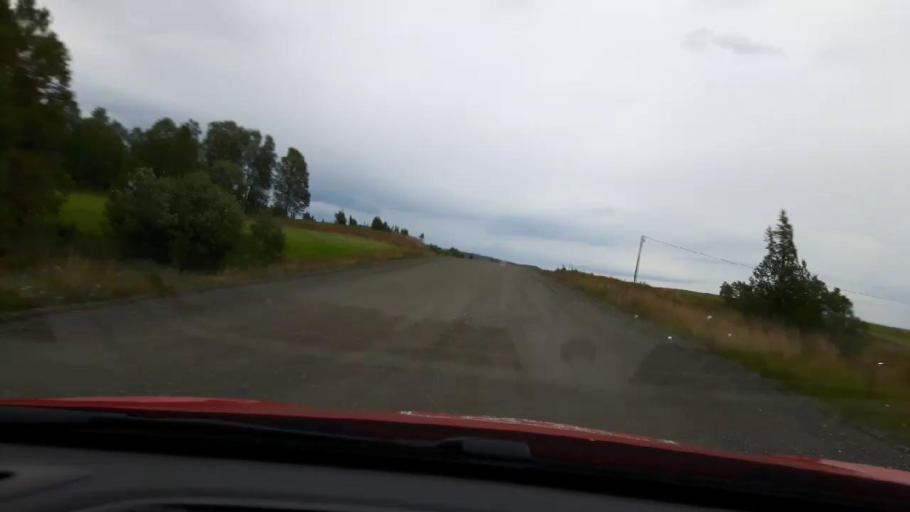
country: NO
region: Nord-Trondelag
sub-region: Meraker
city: Meraker
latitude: 63.5590
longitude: 12.3434
